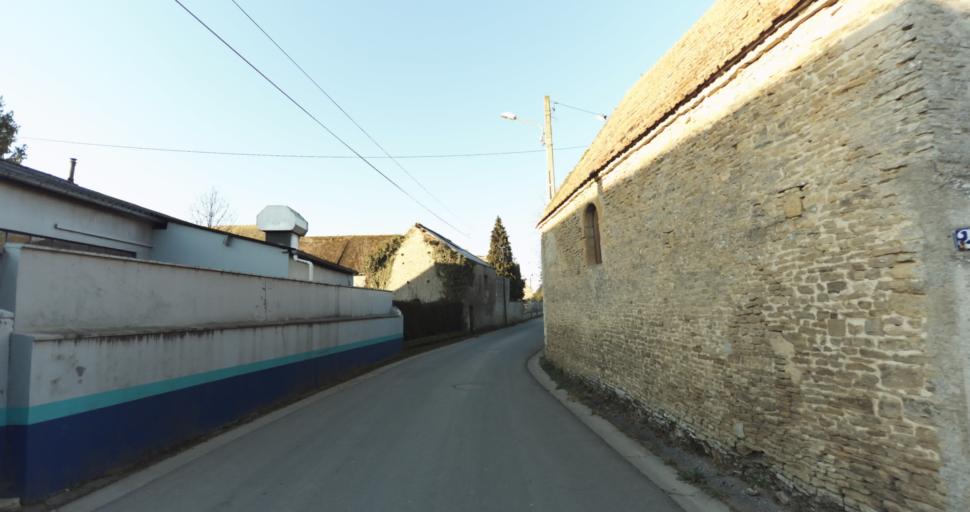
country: FR
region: Lower Normandy
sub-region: Departement du Calvados
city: Saint-Pierre-sur-Dives
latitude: 49.0192
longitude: -0.0447
